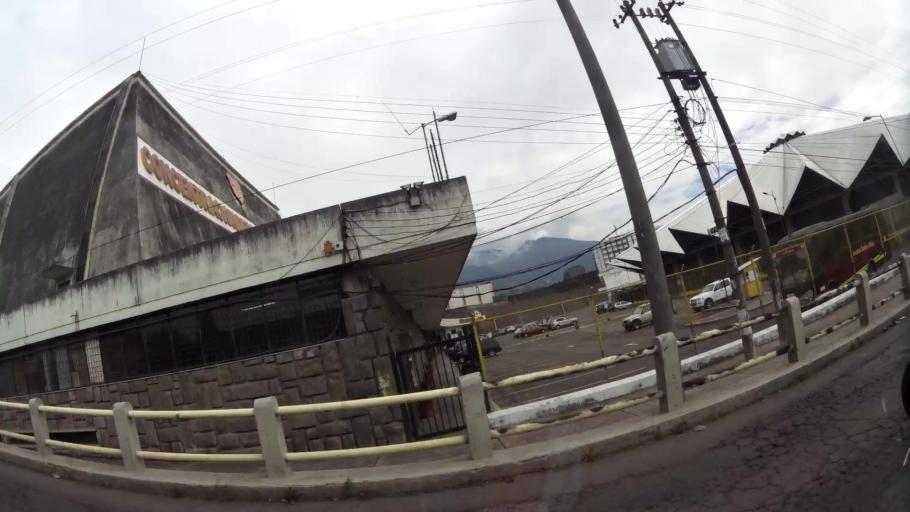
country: EC
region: Pichincha
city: Quito
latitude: -0.2143
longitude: -78.4900
